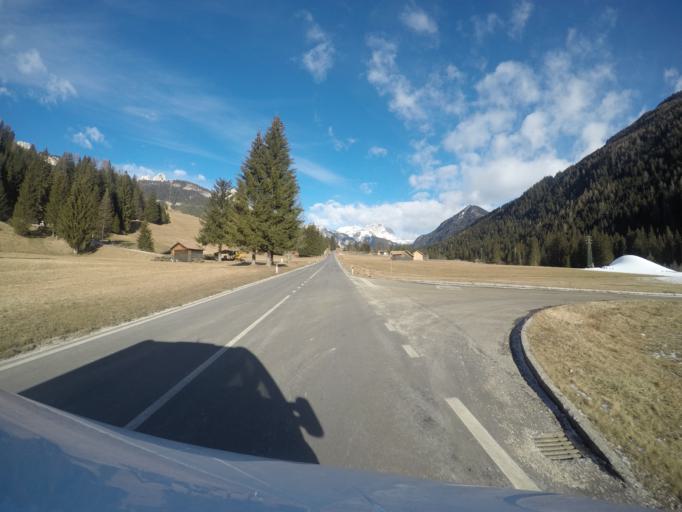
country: IT
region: Trentino-Alto Adige
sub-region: Provincia di Trento
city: Vigo di Fassa
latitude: 46.4102
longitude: 11.6769
